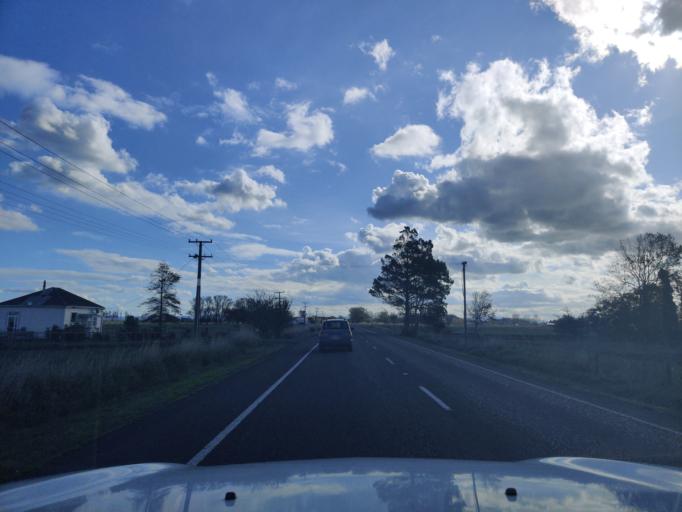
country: NZ
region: Waikato
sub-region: Hauraki District
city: Ngatea
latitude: -37.2832
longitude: 175.5425
